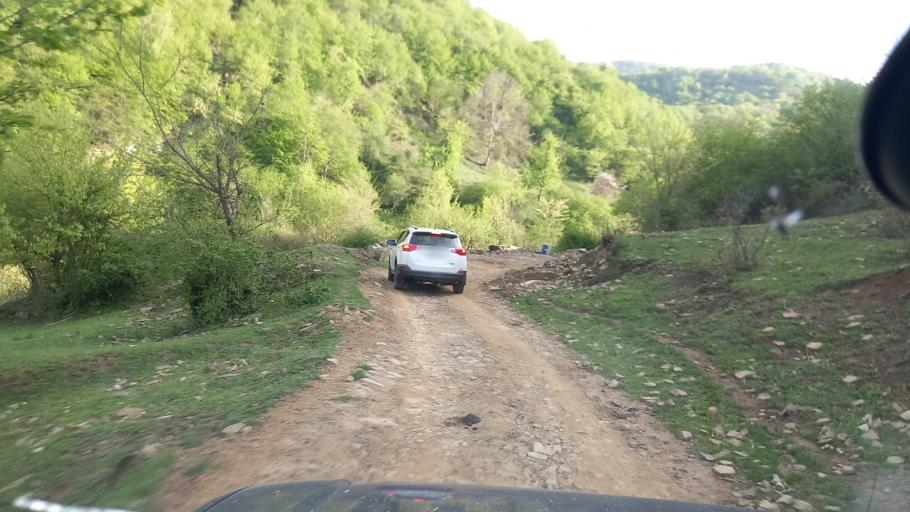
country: RU
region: Dagestan
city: Khuchni
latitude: 41.9451
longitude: 47.8350
